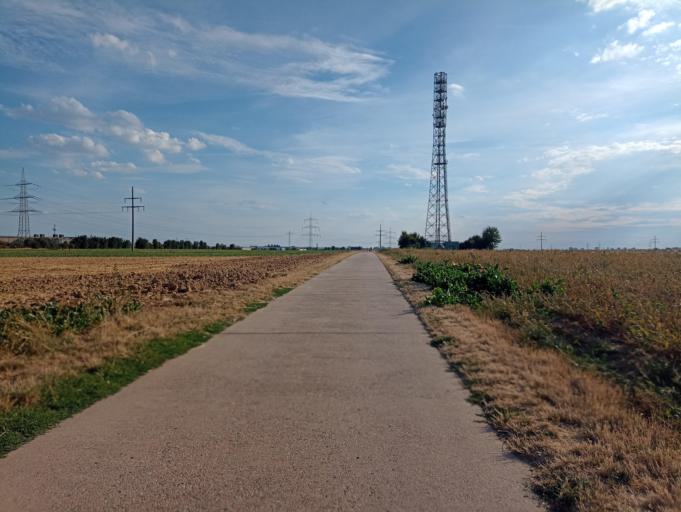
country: DE
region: Hesse
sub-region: Regierungsbezirk Darmstadt
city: Bad Homburg vor der Hoehe
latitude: 50.2003
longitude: 8.6376
